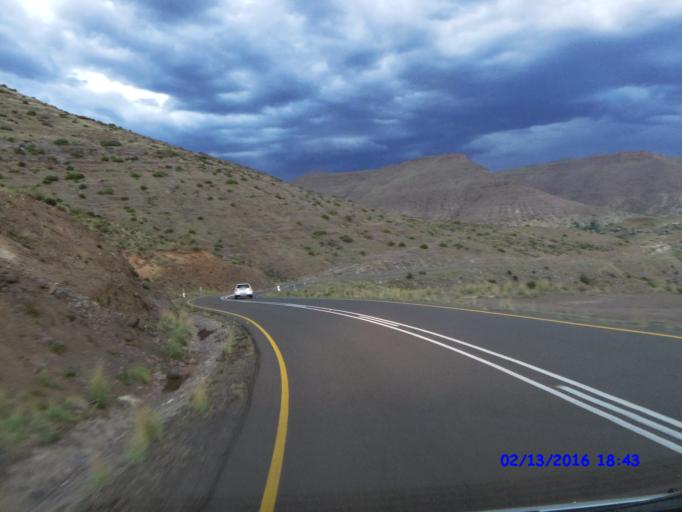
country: LS
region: Qacha's Nek
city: Qacha's Nek
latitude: -30.0471
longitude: 28.3074
